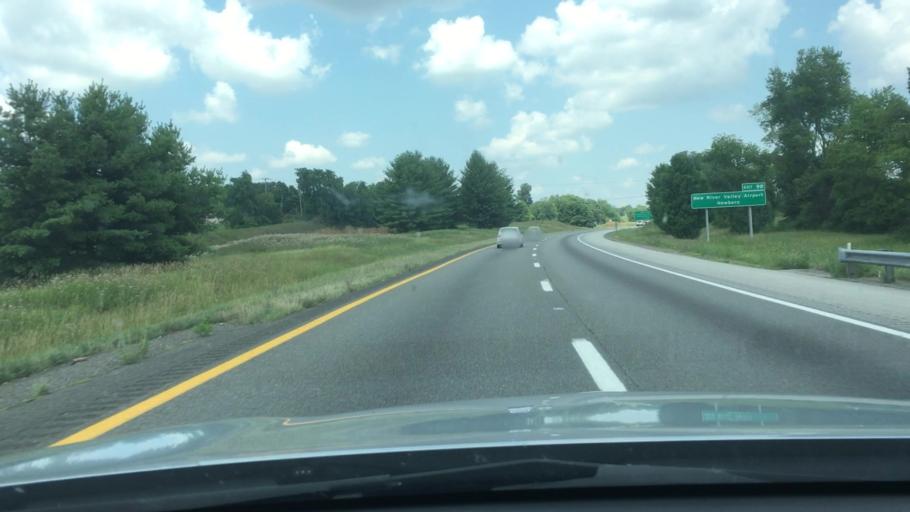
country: US
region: Virginia
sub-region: Pulaski County
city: Dublin
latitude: 37.0728
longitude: -80.7029
